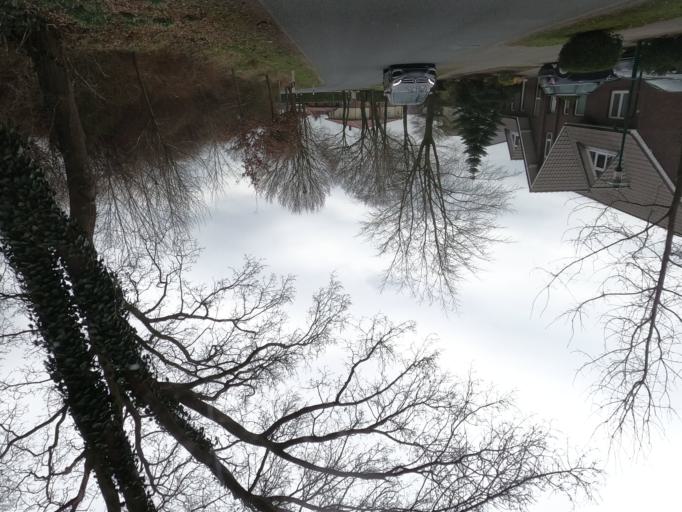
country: DE
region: Lower Saxony
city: Molbergen
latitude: 52.8650
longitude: 7.9241
